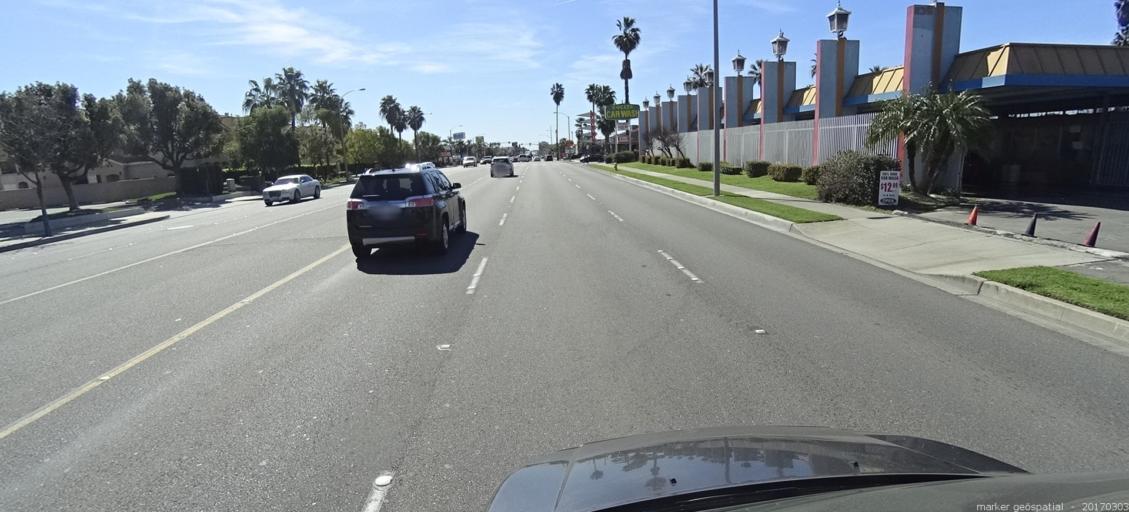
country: US
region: California
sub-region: Orange County
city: Fullerton
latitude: 33.8491
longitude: -117.9418
